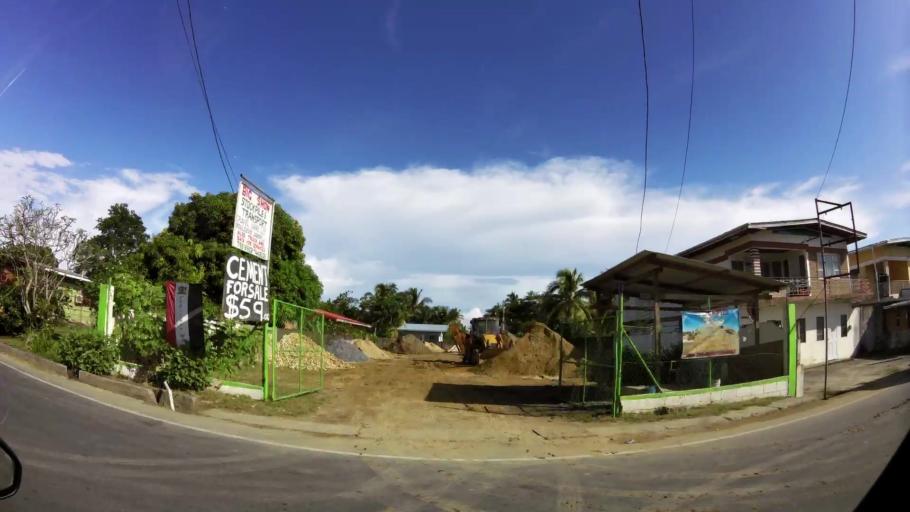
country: TT
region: Chaguanas
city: Chaguanas
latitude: 10.5324
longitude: -61.3801
